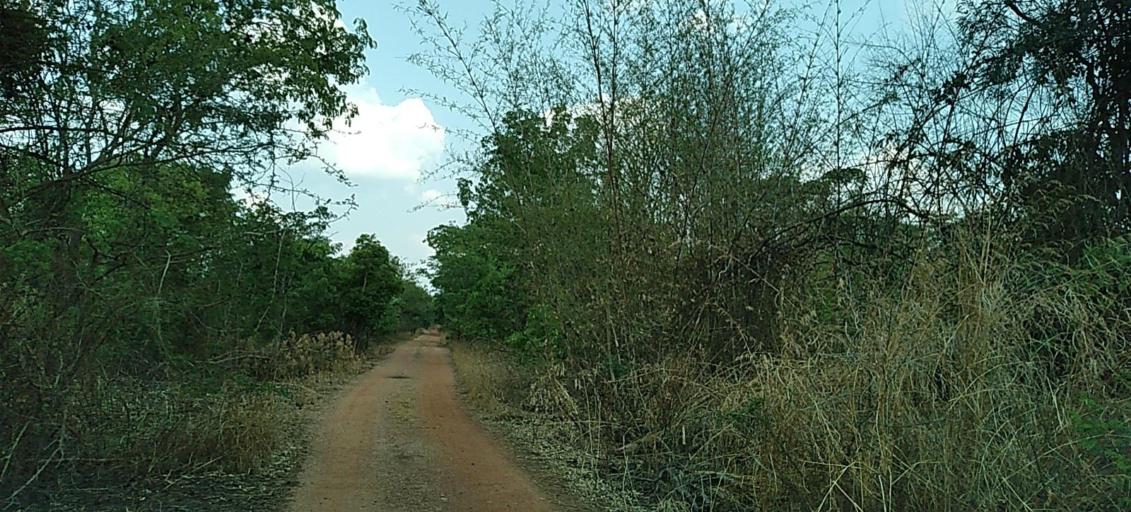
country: ZM
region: Copperbelt
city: Luanshya
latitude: -13.1595
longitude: 28.3351
